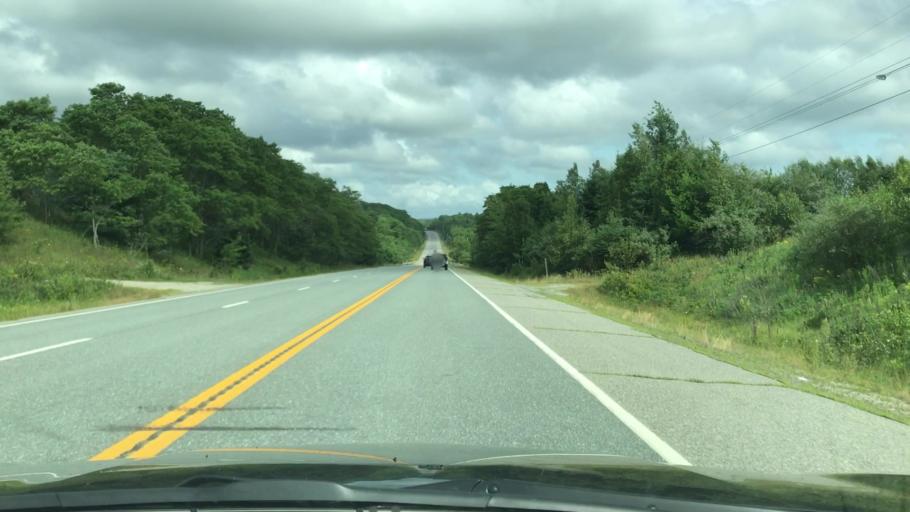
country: US
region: Maine
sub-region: Hancock County
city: Orland
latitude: 44.5667
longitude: -68.6160
